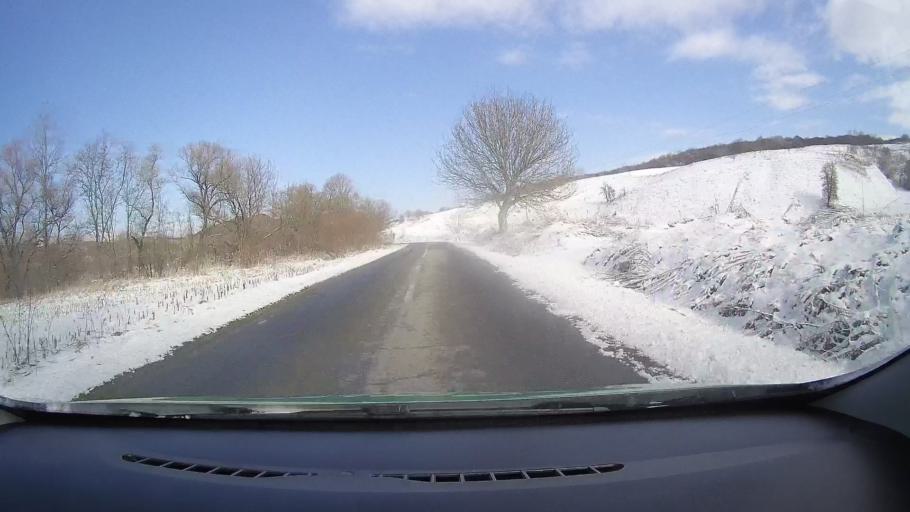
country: RO
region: Sibiu
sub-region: Comuna Mihaileni
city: Mihaileni
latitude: 45.9945
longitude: 24.3565
